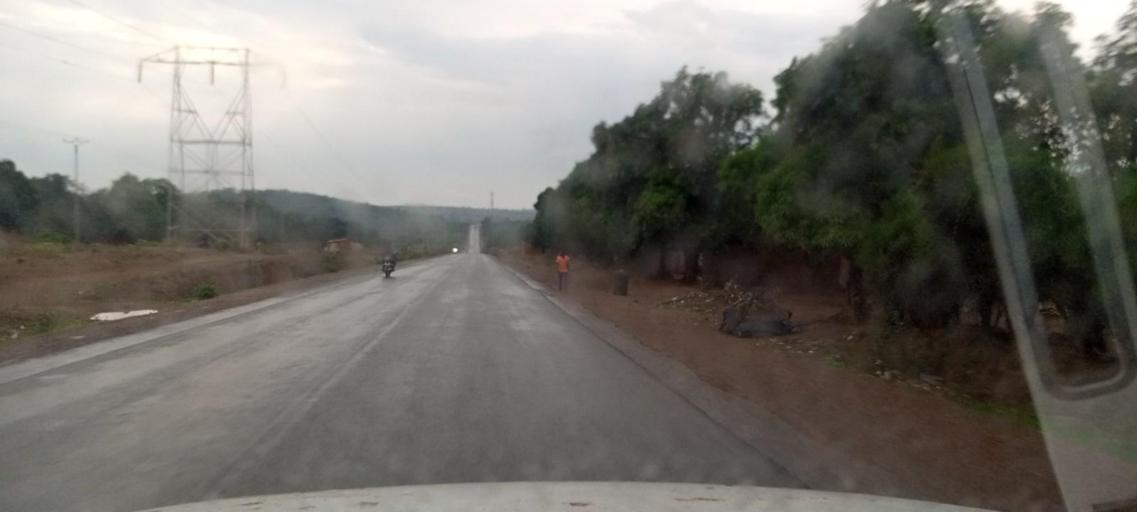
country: CD
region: Katanga
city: Likasi
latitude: -11.0007
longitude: 26.8807
